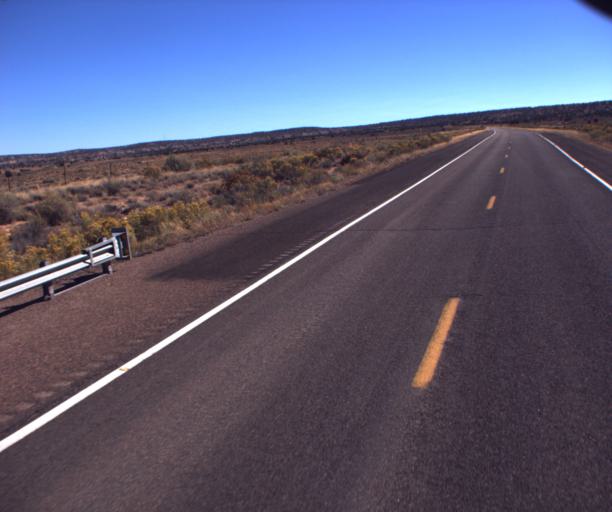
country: US
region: Arizona
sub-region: Navajo County
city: First Mesa
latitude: 35.7546
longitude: -110.1368
